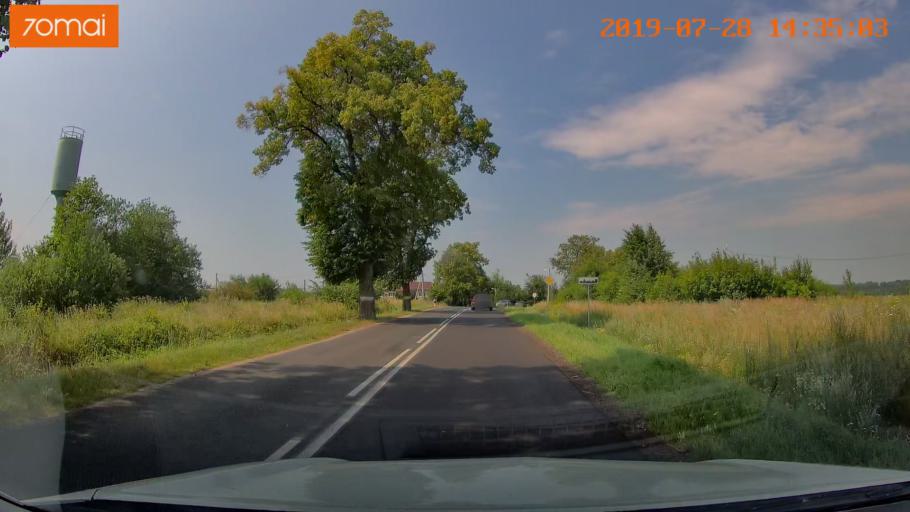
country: RU
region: Kaliningrad
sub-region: Gorod Kaliningrad
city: Yantarnyy
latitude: 54.8288
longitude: 20.0117
